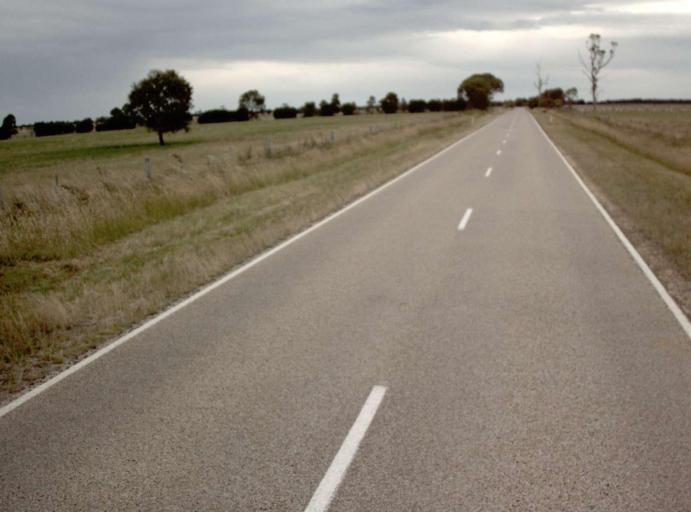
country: AU
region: Victoria
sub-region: East Gippsland
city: Bairnsdale
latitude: -37.9539
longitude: 147.5117
